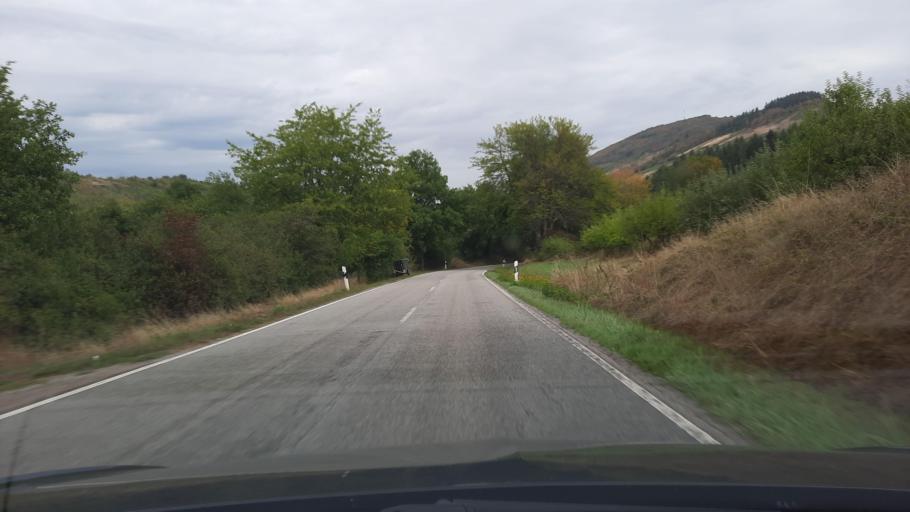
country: DE
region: Rheinland-Pfalz
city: Klusserath
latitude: 49.8583
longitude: 6.8427
